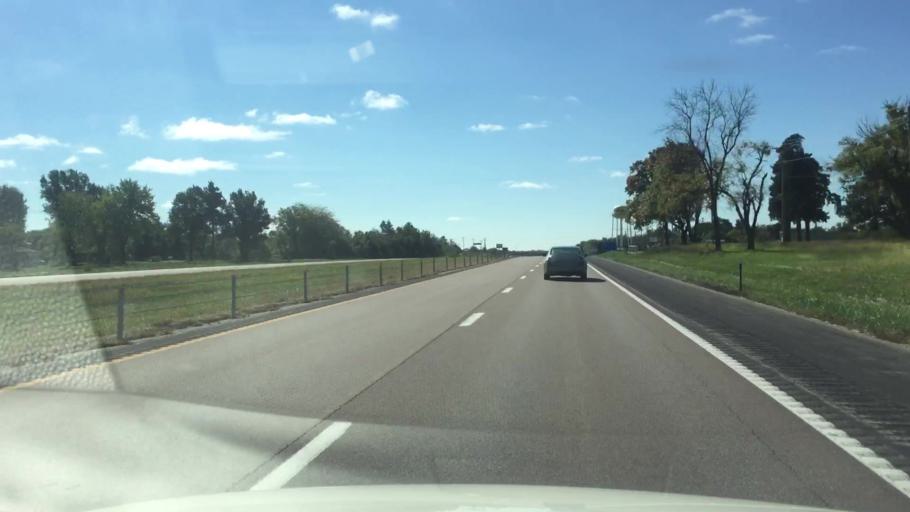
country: US
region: Missouri
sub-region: Boone County
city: Ashland
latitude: 38.7854
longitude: -92.2524
